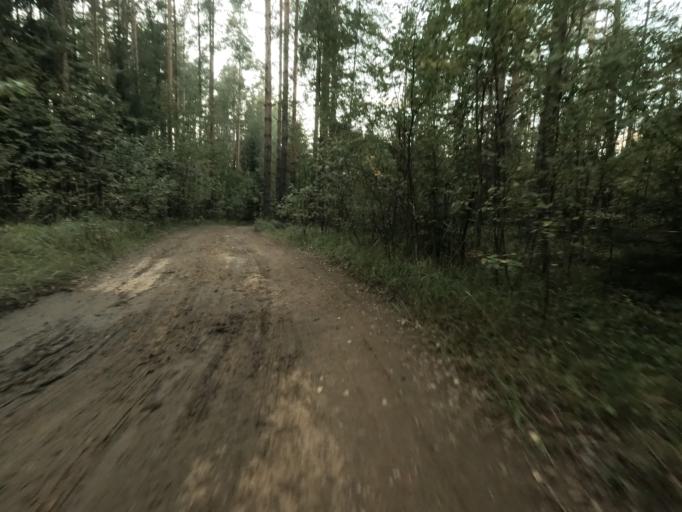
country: RU
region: Leningrad
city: Otradnoye
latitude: 59.8460
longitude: 30.7988
